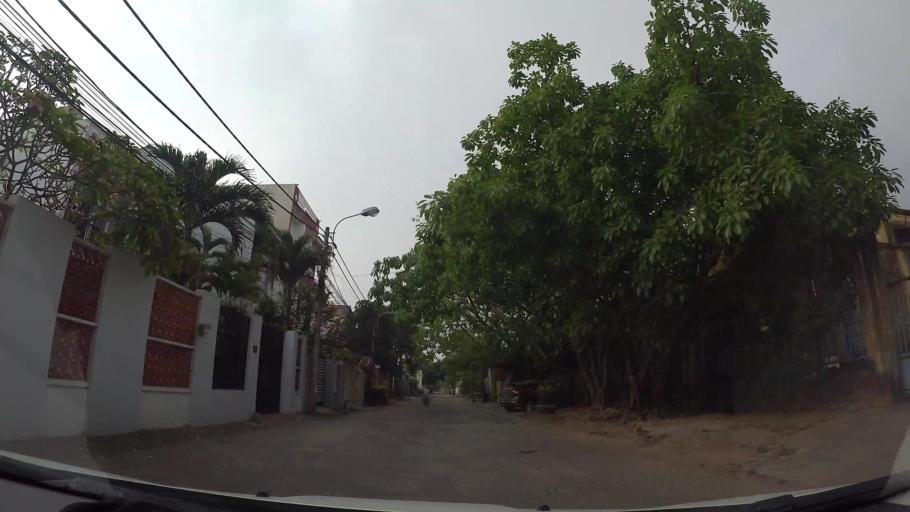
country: VN
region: Da Nang
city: Son Tra
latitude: 16.0802
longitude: 108.2393
